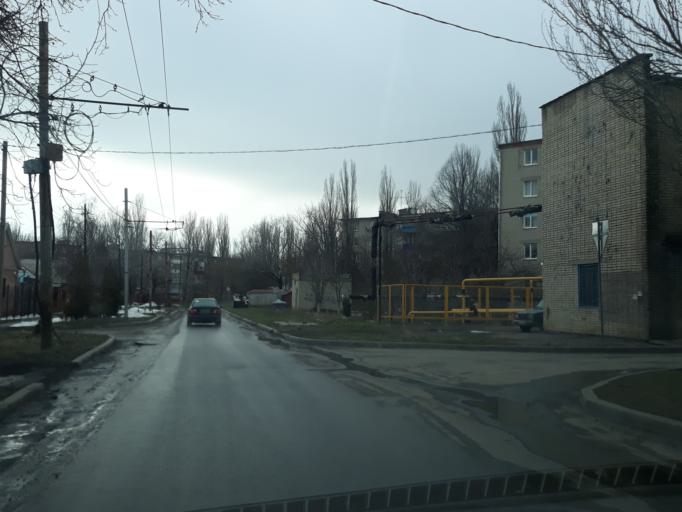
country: RU
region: Rostov
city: Taganrog
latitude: 47.2625
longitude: 38.9245
